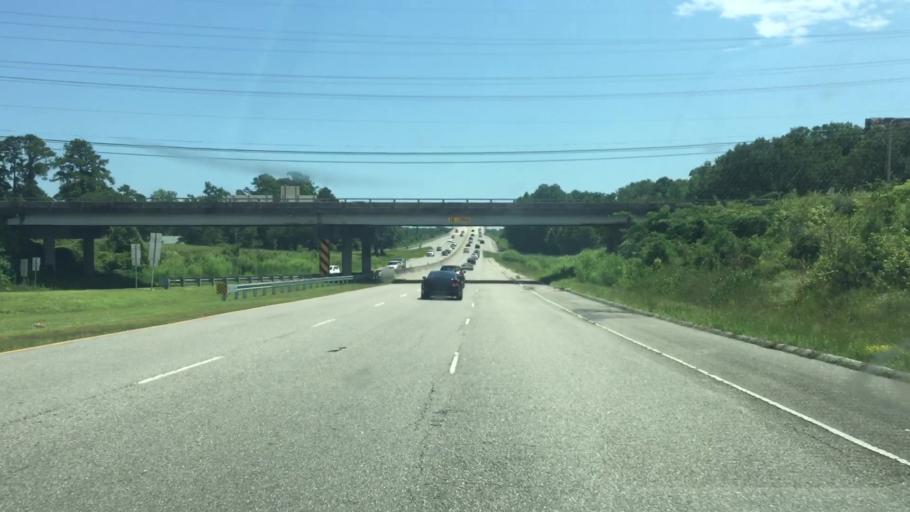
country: US
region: South Carolina
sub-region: Horry County
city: Little River
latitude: 33.8597
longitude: -78.6571
